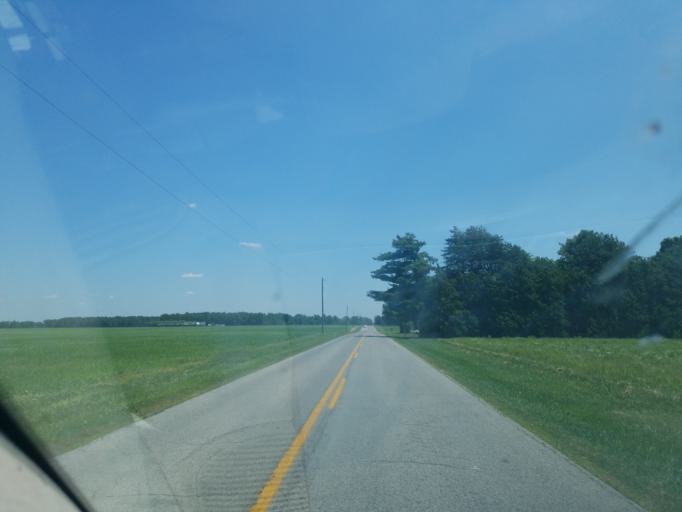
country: US
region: Ohio
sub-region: Allen County
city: Delphos
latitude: 40.7868
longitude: -84.2879
